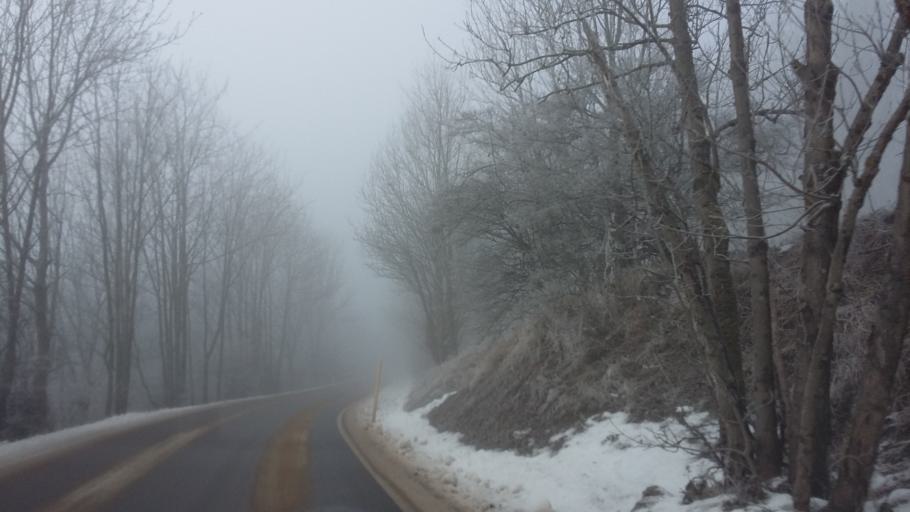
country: CZ
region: Liberecky
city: Rovensko pod Troskami
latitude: 50.5835
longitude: 15.2752
